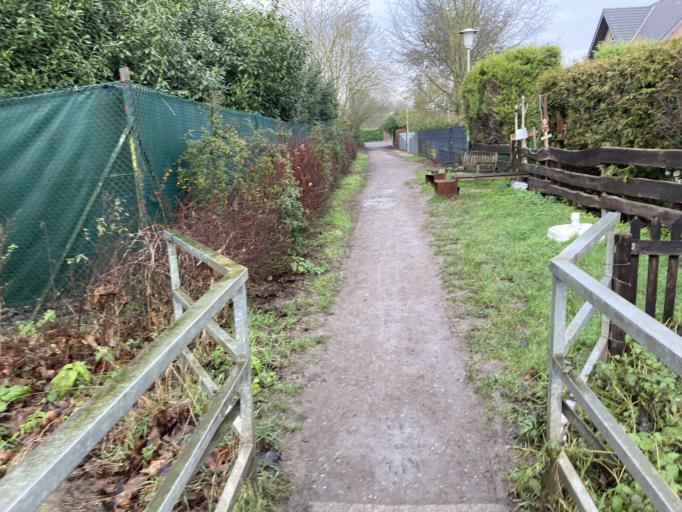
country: DE
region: North Rhine-Westphalia
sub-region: Regierungsbezirk Dusseldorf
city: Neubrueck
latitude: 51.1209
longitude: 6.6226
